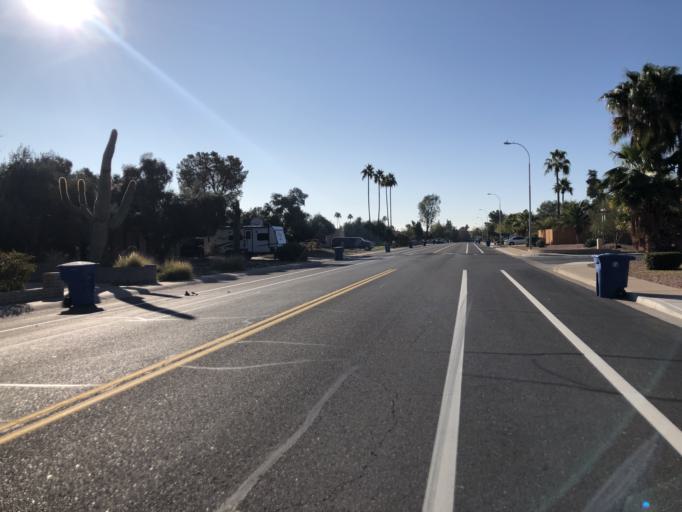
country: US
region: Arizona
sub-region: Maricopa County
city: Chandler
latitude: 33.3022
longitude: -111.9199
